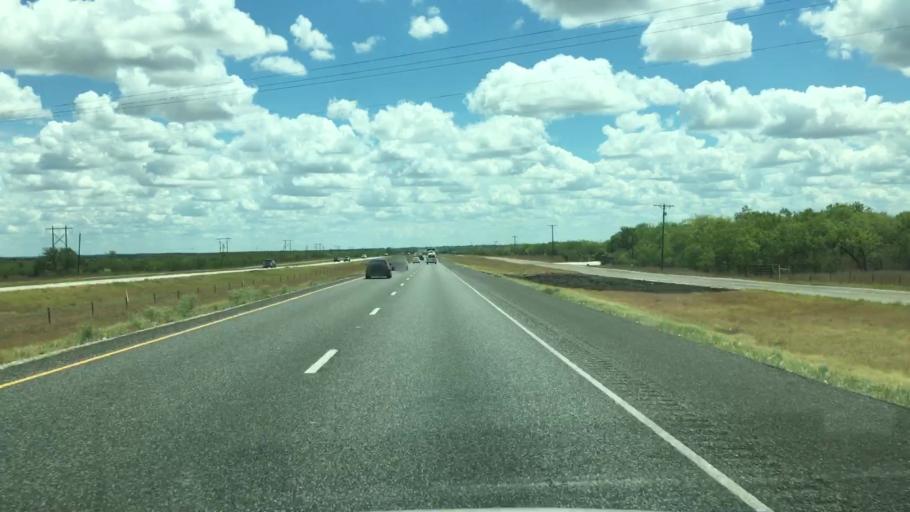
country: US
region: Texas
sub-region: Atascosa County
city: Pleasanton
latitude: 28.8650
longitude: -98.3903
